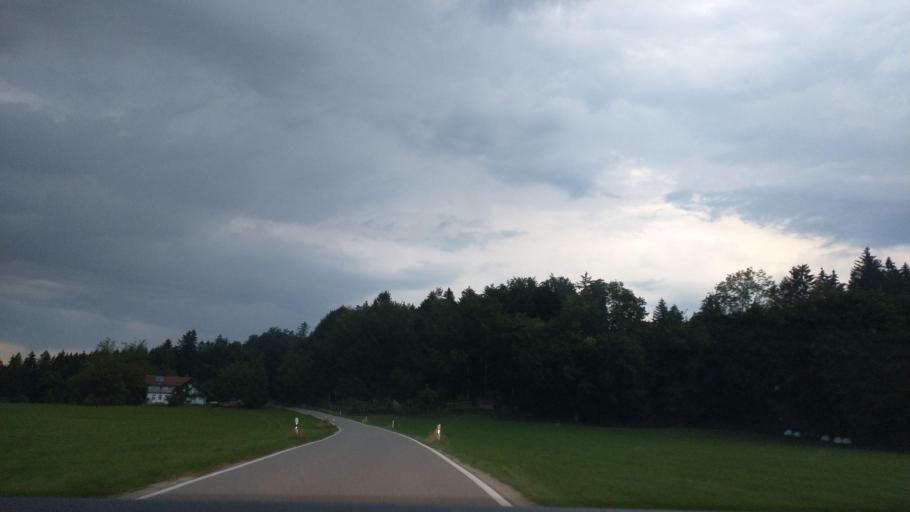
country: DE
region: Baden-Wuerttemberg
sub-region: Tuebingen Region
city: Amtzell
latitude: 47.6897
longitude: 9.7413
